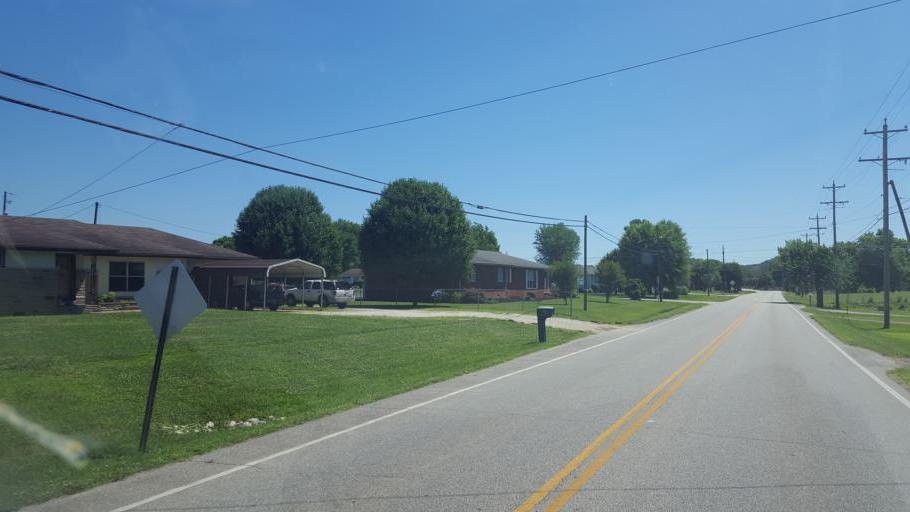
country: US
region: West Virginia
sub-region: Cabell County
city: Pea Ridge
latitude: 38.4411
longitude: -82.3525
